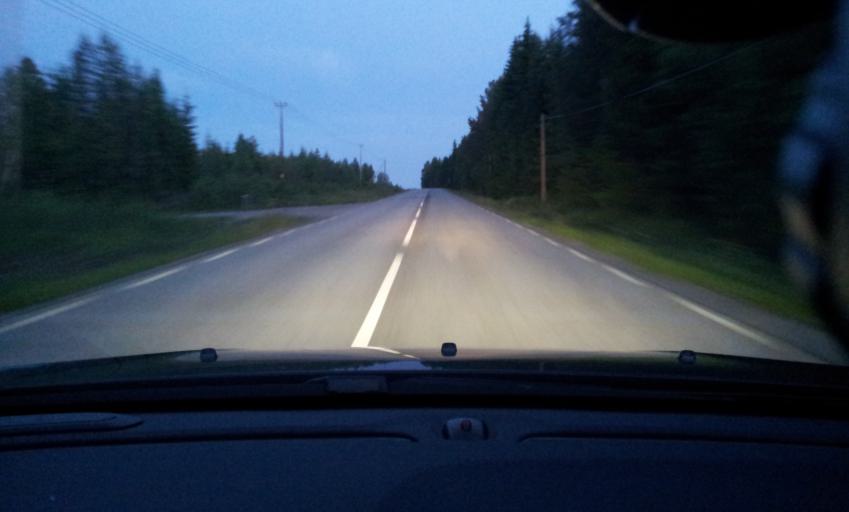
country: SE
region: Jaemtland
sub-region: OEstersunds Kommun
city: Brunflo
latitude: 62.7634
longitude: 14.9918
